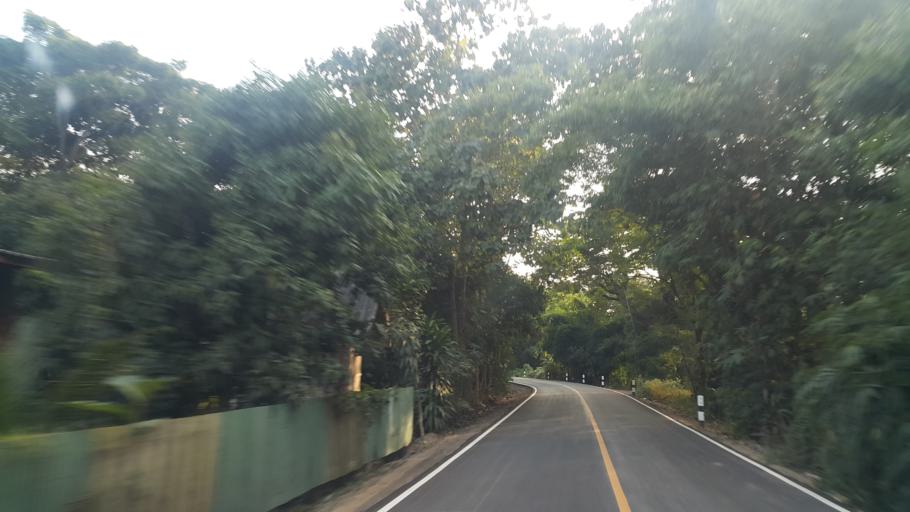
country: TH
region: Lampang
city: Sop Prap
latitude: 17.9393
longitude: 99.3412
